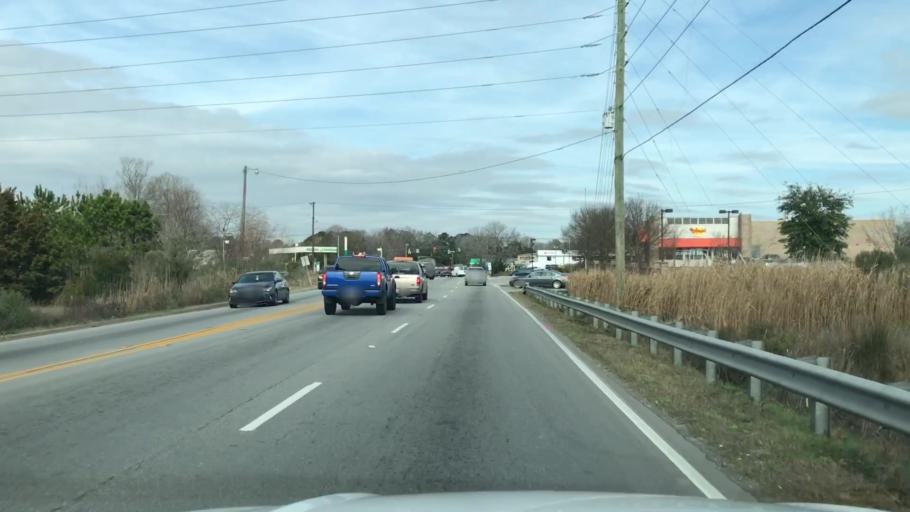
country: US
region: South Carolina
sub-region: Charleston County
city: Shell Point
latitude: 32.8005
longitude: -80.1086
